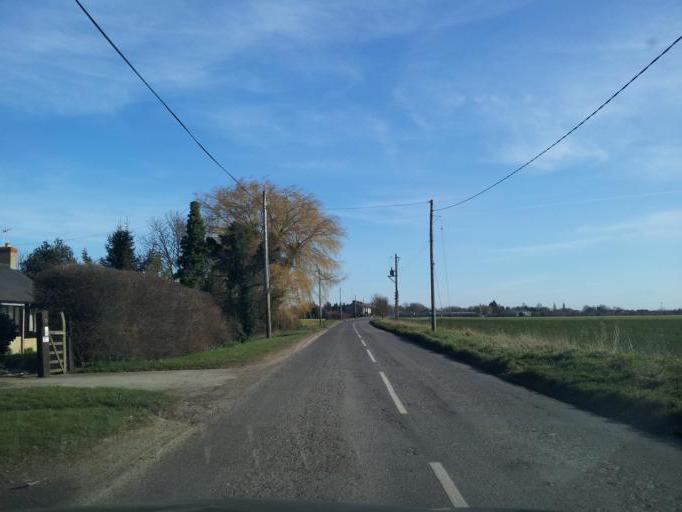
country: GB
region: England
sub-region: Cambridgeshire
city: Meldreth
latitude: 52.1186
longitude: 0.0256
